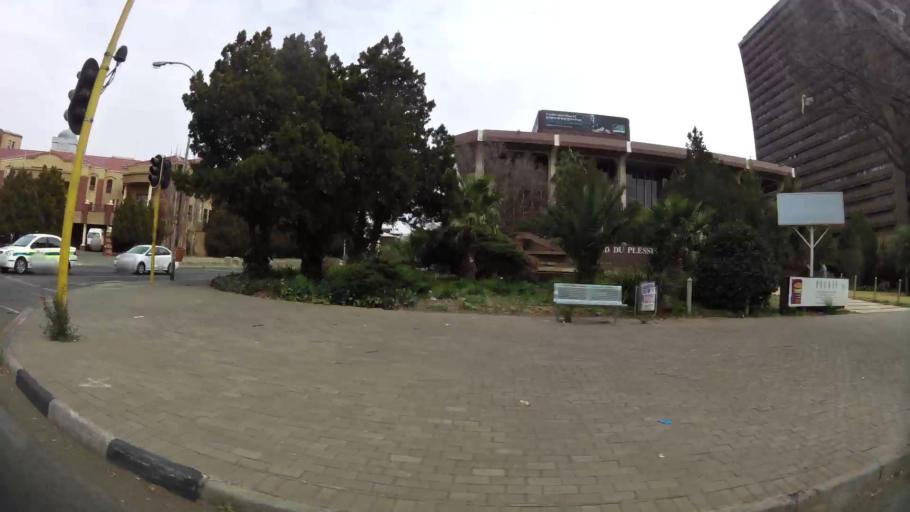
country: ZA
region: Orange Free State
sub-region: Mangaung Metropolitan Municipality
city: Bloemfontein
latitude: -29.1166
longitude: 26.2138
